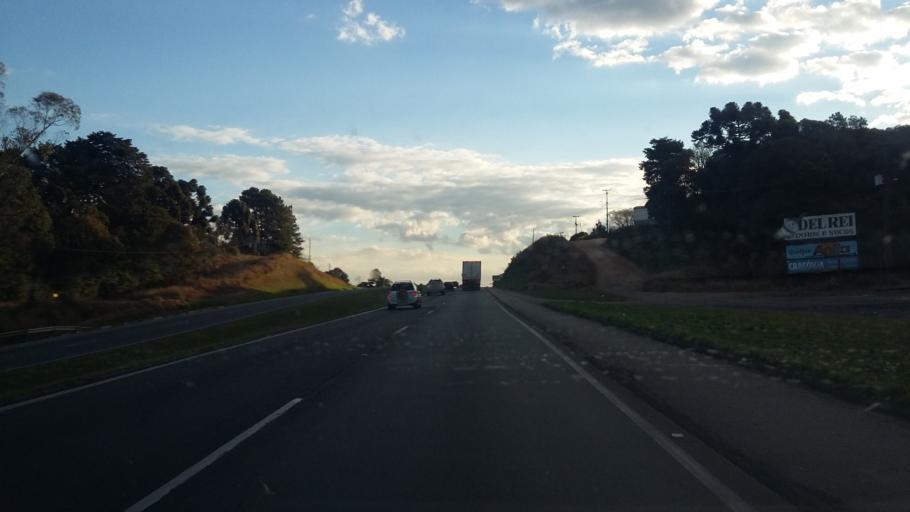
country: BR
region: Parana
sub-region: Campo Largo
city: Campo Largo
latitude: -25.4311
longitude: -49.4261
